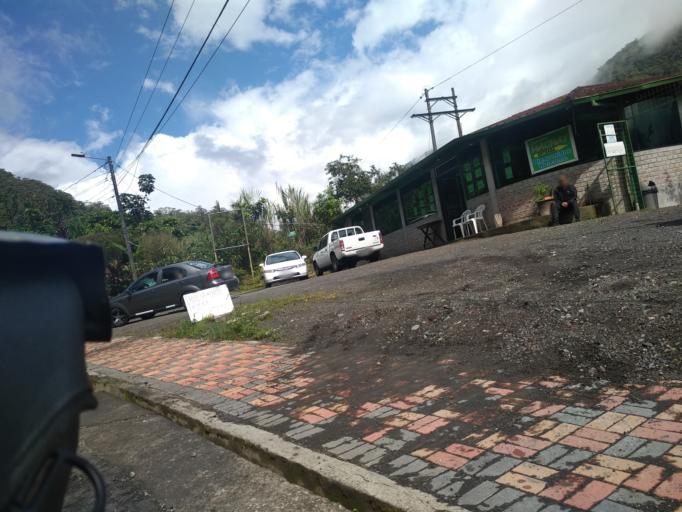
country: EC
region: Tungurahua
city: Banos
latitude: -1.4023
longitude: -78.2837
